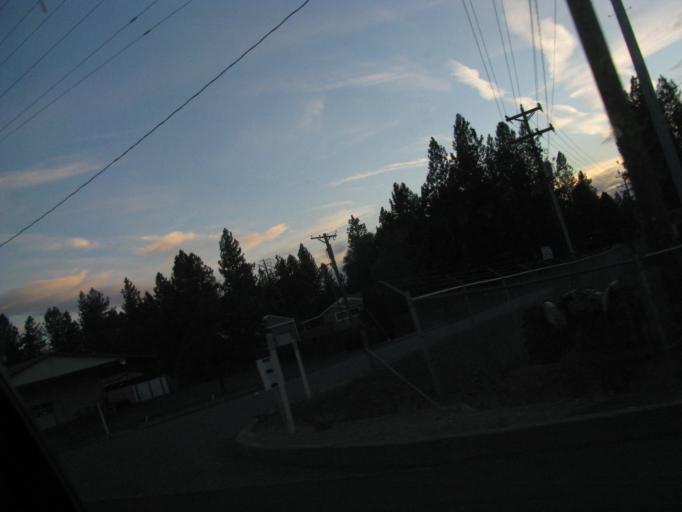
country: US
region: Washington
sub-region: Spokane County
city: Mead
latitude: 47.7984
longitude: -117.3500
